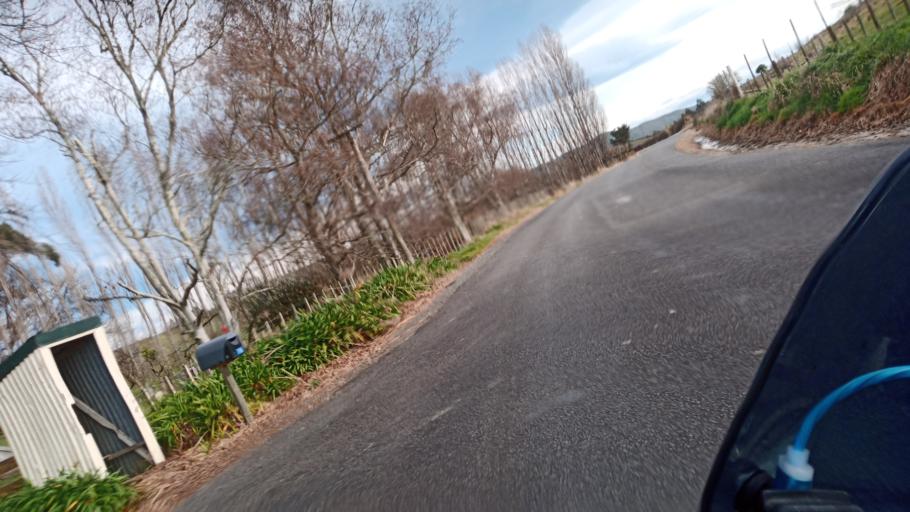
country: NZ
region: Hawke's Bay
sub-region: Wairoa District
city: Wairoa
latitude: -38.9737
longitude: 177.4308
